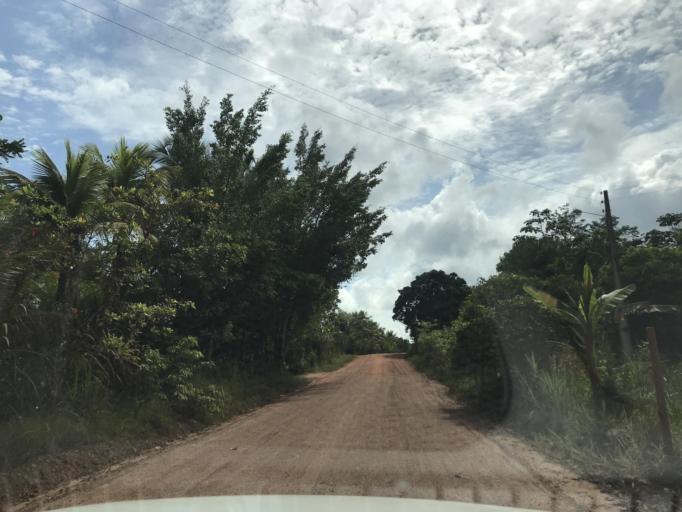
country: BR
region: Bahia
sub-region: Entre Rios
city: Entre Rios
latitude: -12.1711
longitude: -38.1472
